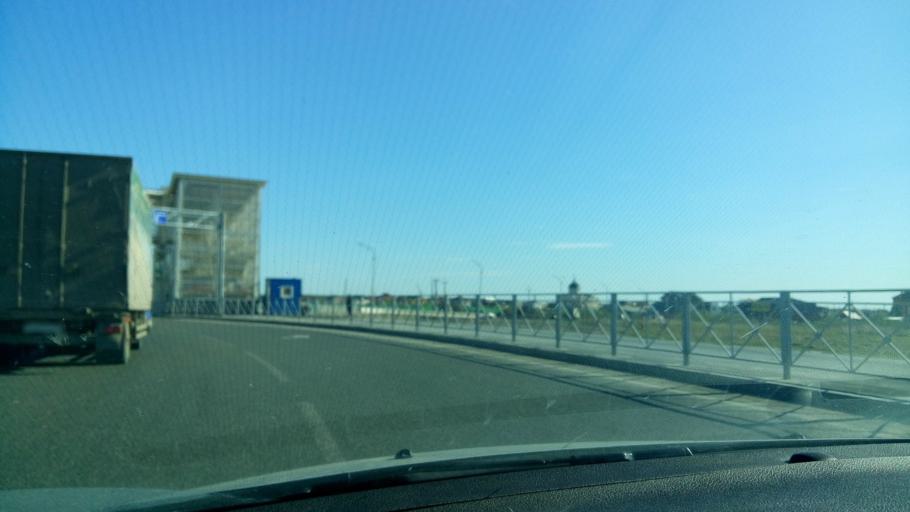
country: RU
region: Tjumen
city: Tyumen
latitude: 57.1049
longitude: 65.5603
